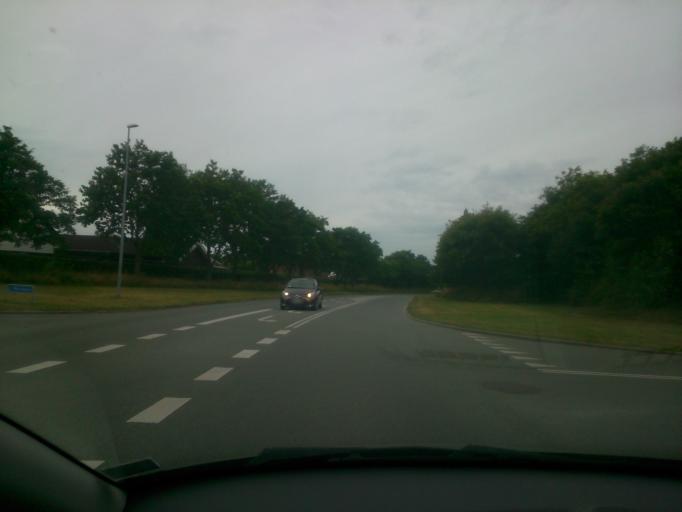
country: DK
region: South Denmark
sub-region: Esbjerg Kommune
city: Esbjerg
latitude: 55.5152
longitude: 8.4203
